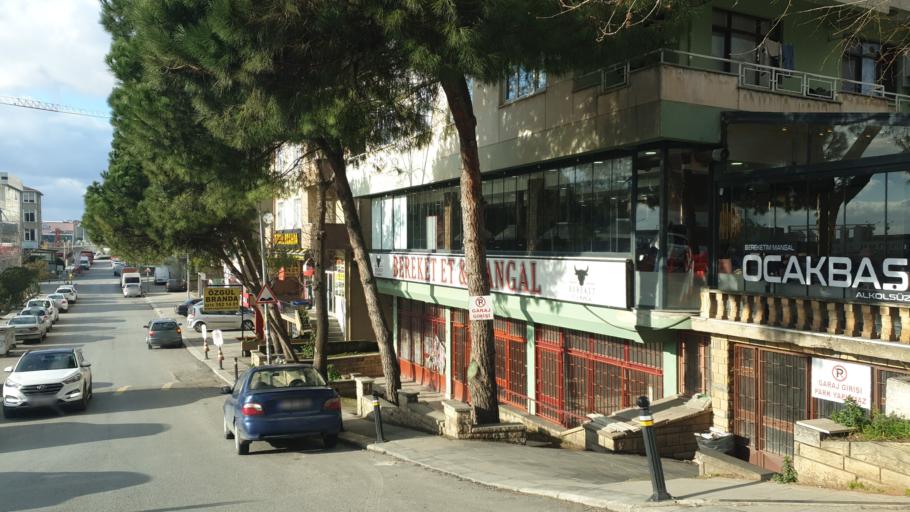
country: TR
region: Istanbul
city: Icmeler
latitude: 40.8475
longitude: 29.3020
